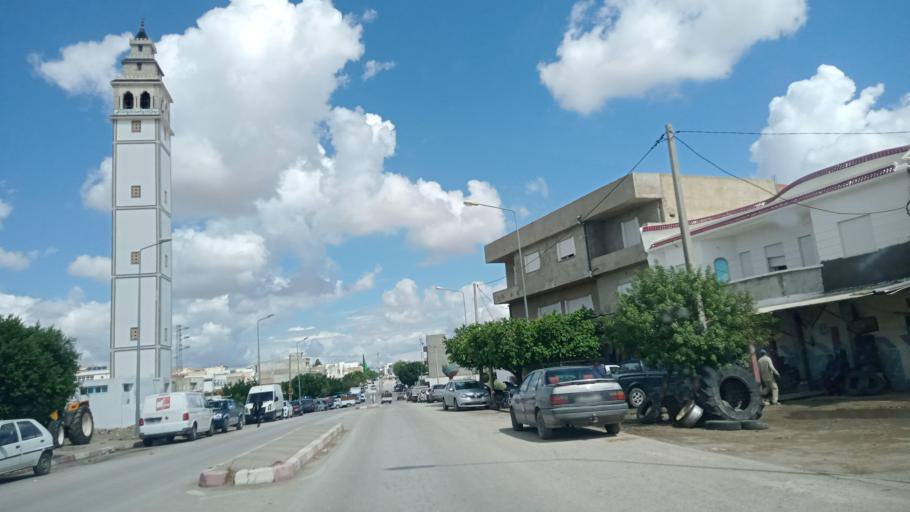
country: TN
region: Silyanah
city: Al Karib
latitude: 36.3239
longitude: 9.1309
